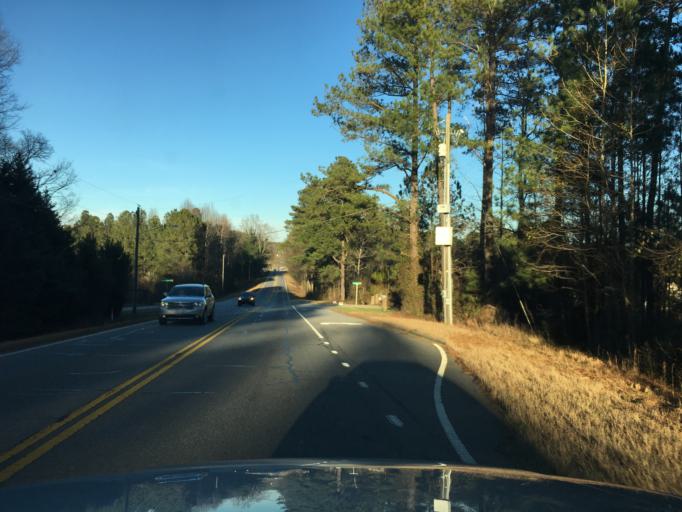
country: US
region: Georgia
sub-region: Barrow County
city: Winder
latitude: 33.9116
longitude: -83.7870
